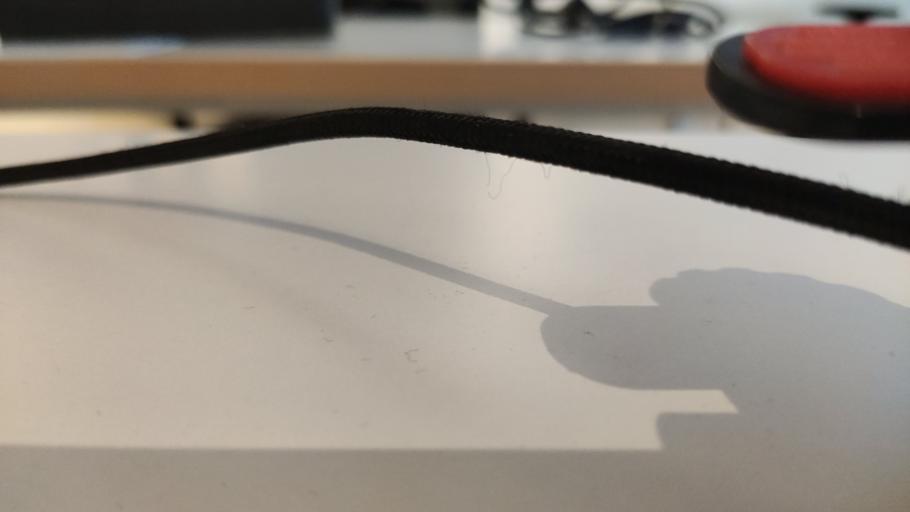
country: RU
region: Moskovskaya
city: Ruza
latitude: 55.8134
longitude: 36.2969
